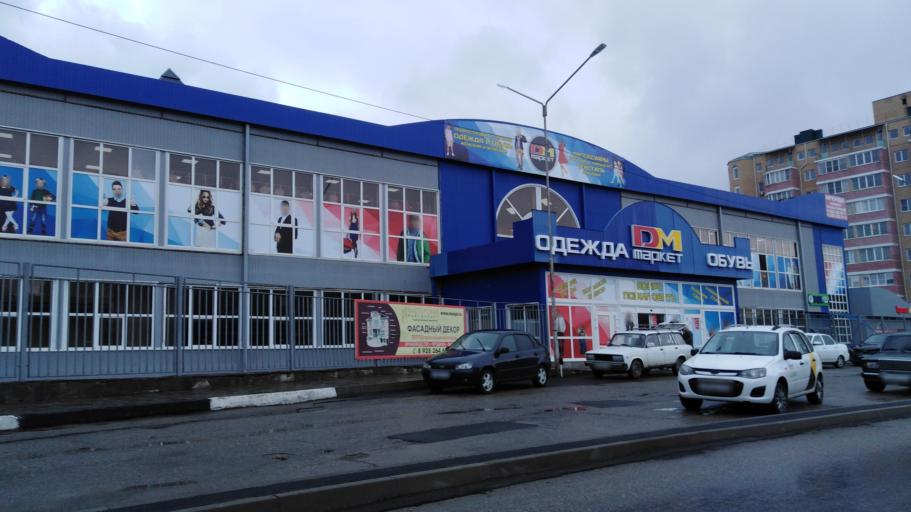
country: RU
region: Stavropol'skiy
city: Yessentukskaya
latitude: 44.0465
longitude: 42.8973
